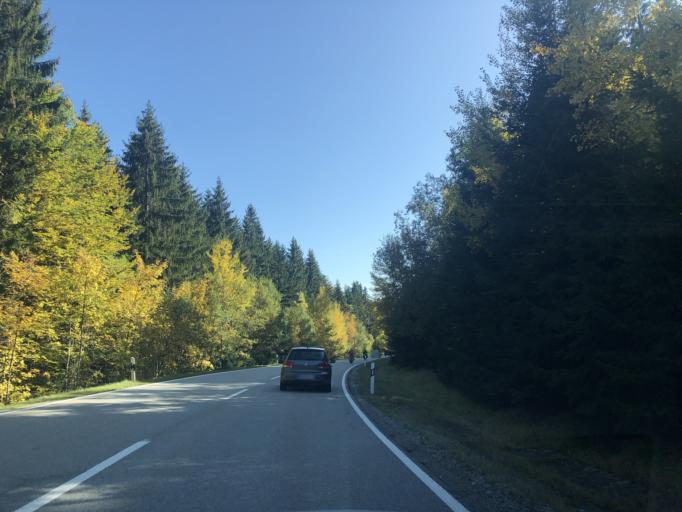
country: DE
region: Bavaria
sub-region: Lower Bavaria
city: Langdorf
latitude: 49.0273
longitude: 13.1281
